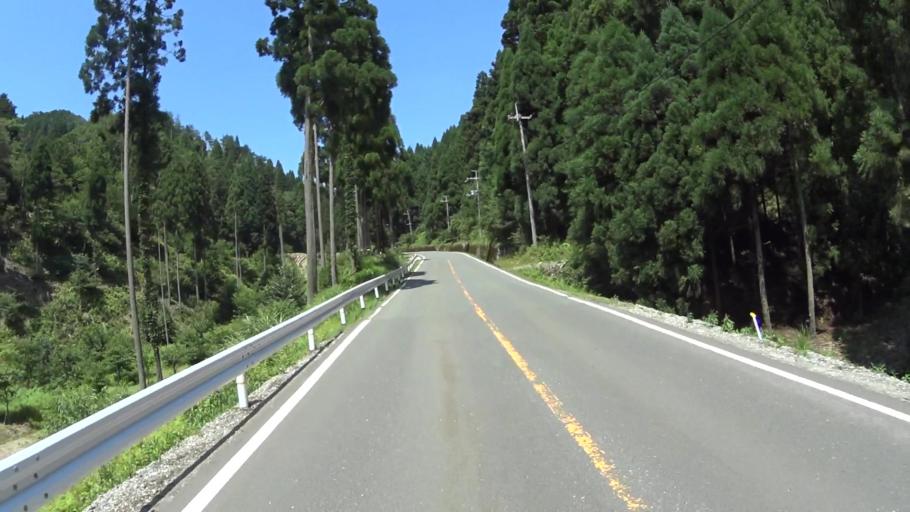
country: JP
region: Fukui
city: Obama
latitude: 35.3835
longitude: 135.9252
